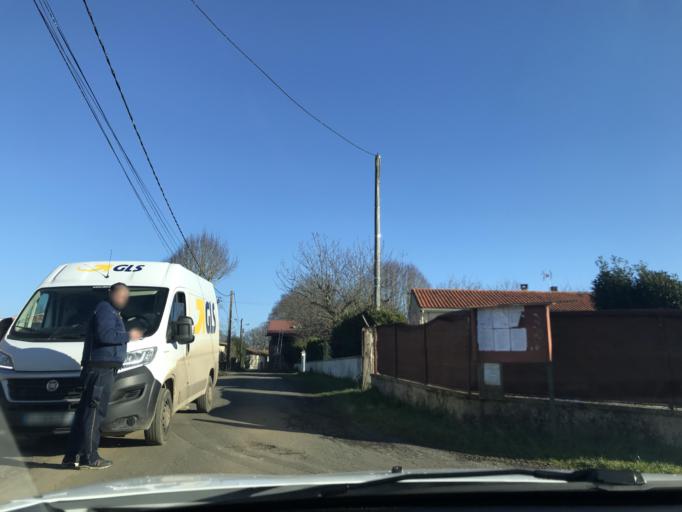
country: FR
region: Poitou-Charentes
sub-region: Departement de la Charente
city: Chasseneuil-sur-Bonnieure
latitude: 45.8451
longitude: 0.5157
